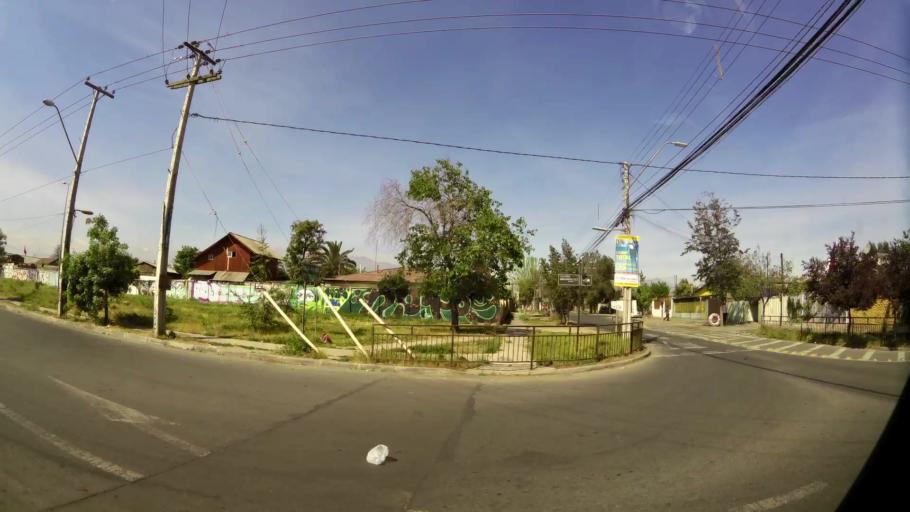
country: CL
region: Santiago Metropolitan
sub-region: Provincia de Maipo
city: San Bernardo
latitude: -33.5357
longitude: -70.6753
